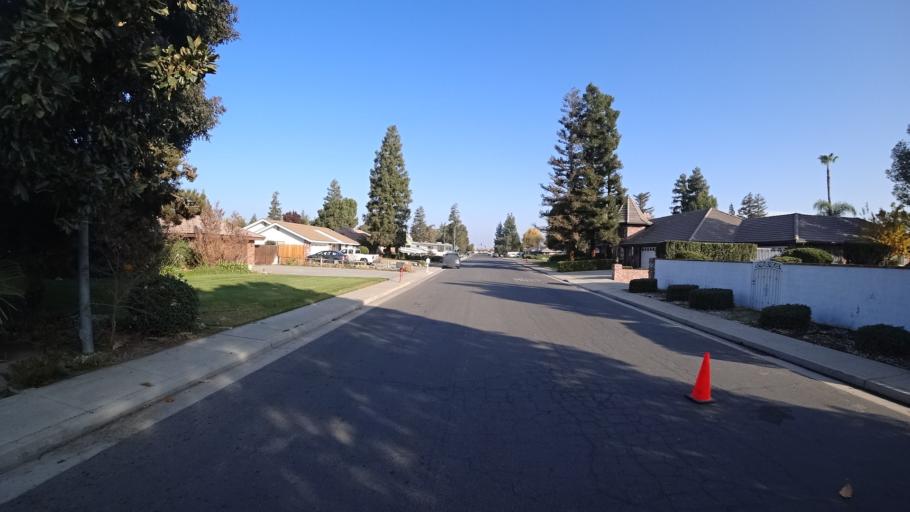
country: US
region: California
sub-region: Kern County
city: Rosedale
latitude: 35.3566
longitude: -119.1486
